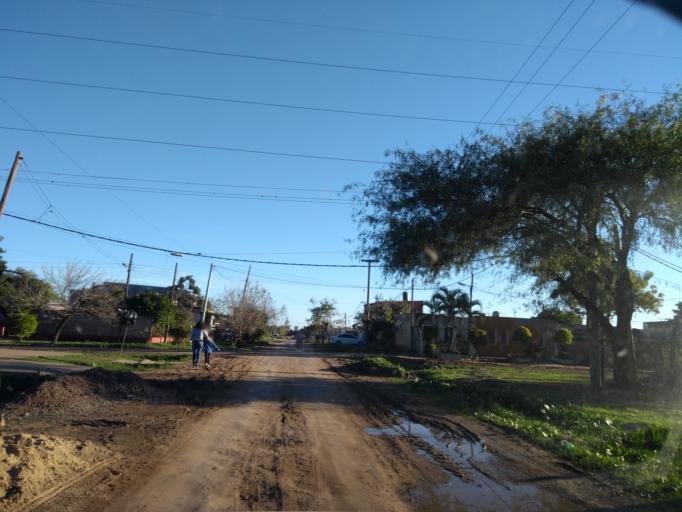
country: AR
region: Chaco
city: Barranqueras
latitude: -27.4905
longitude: -58.9359
